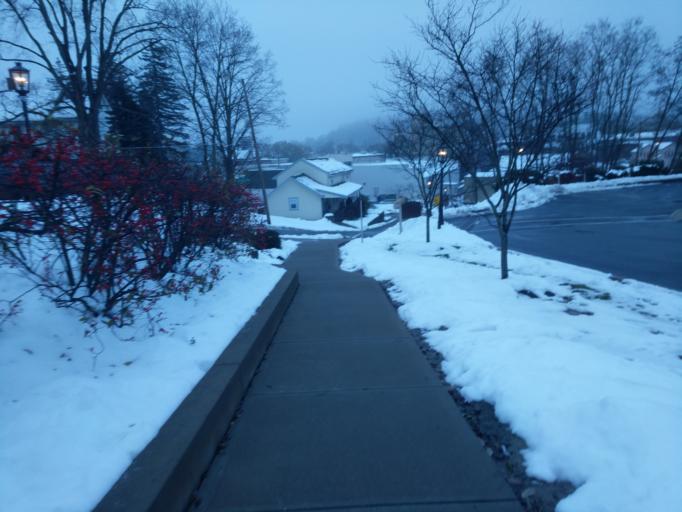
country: US
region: Pennsylvania
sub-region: Tioga County
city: Wellsboro
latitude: 41.7502
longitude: -77.3029
